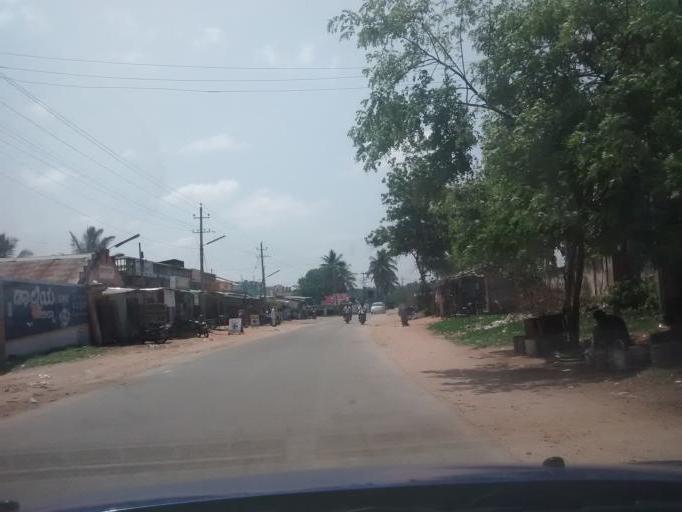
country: IN
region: Karnataka
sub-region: Hassan
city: Konanur
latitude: 12.5632
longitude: 76.2627
